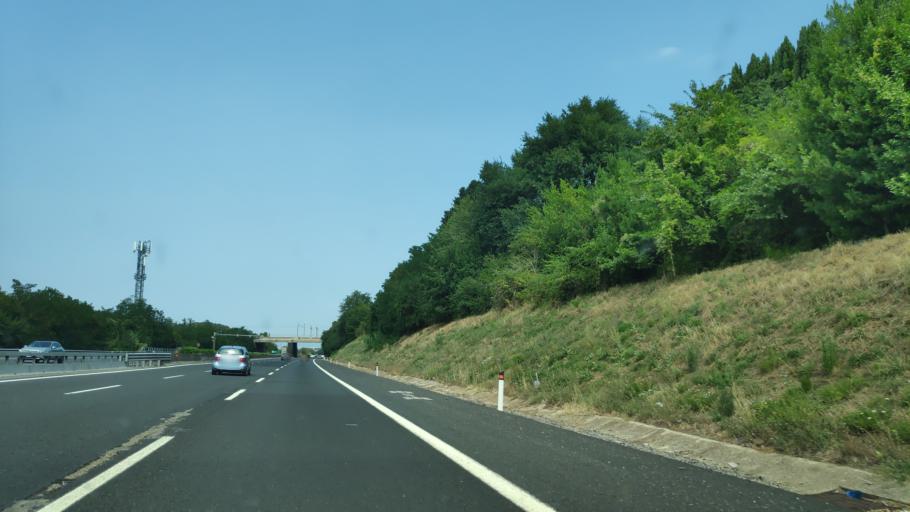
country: IT
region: Latium
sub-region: Citta metropolitana di Roma Capitale
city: San Cesareo
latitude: 41.8262
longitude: 12.8036
